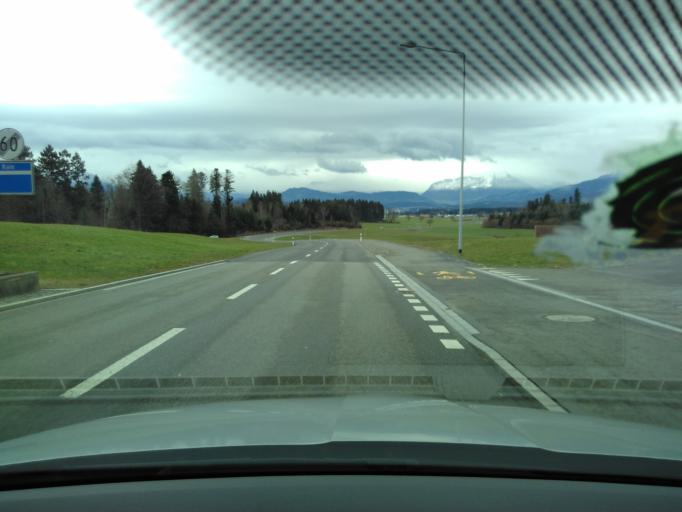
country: CH
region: Lucerne
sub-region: Sursee District
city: Hildisrieden
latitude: 47.1459
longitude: 8.2342
